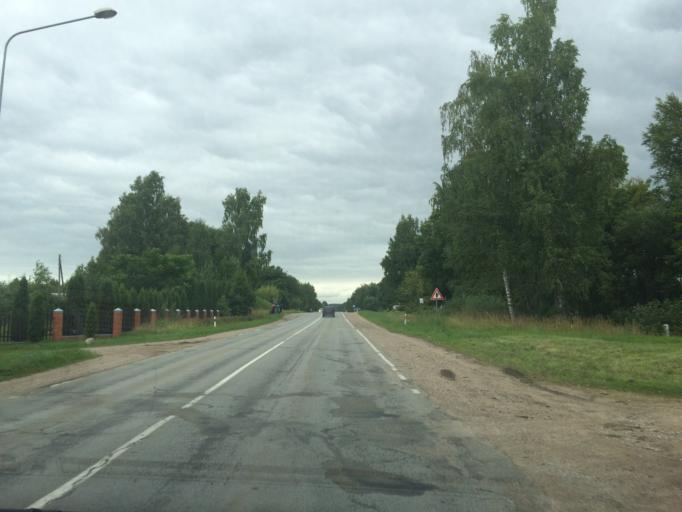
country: LV
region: Rezekne
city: Rezekne
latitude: 56.5475
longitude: 27.3559
